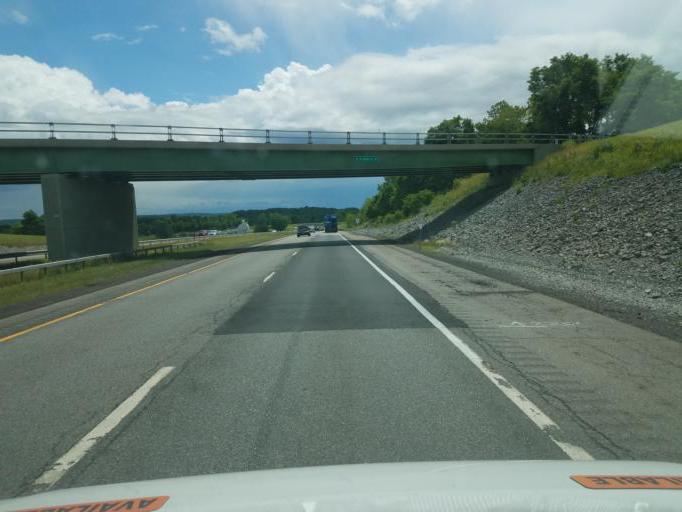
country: US
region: New York
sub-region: Monroe County
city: Pittsford
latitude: 43.0339
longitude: -77.5243
